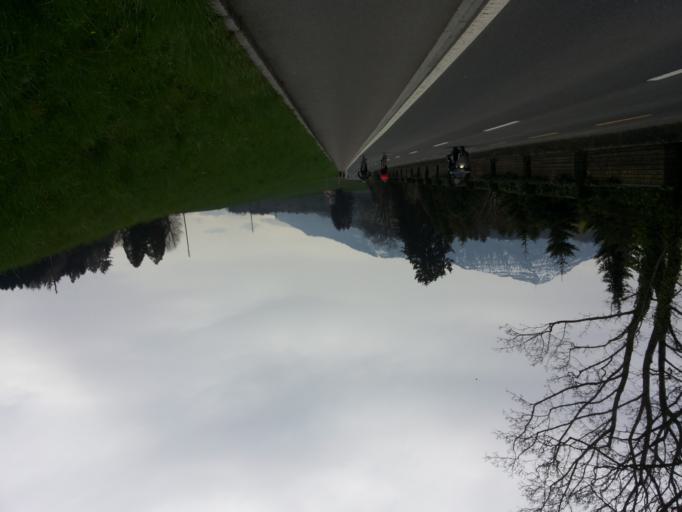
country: CH
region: Lucerne
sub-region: Lucerne-Land District
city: Meierskappel
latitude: 47.1228
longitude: 8.4624
